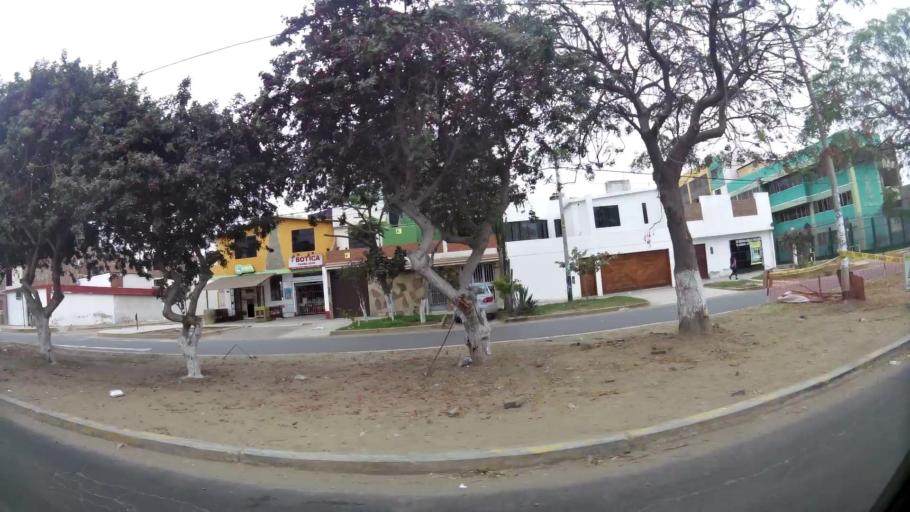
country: PE
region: La Libertad
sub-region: Provincia de Trujillo
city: Trujillo
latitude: -8.1217
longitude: -79.0424
